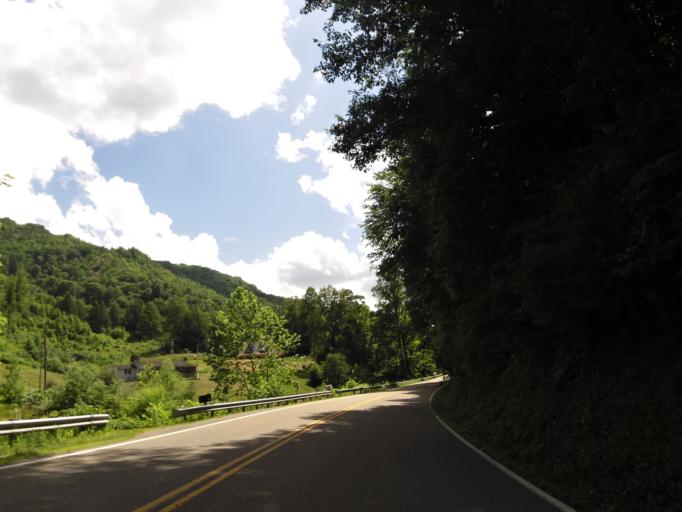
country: US
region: Virginia
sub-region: Lee County
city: Pennington Gap
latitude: 36.7666
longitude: -83.0769
